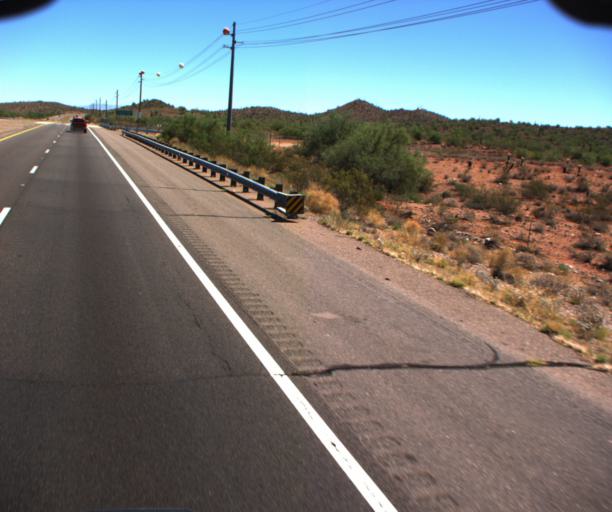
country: US
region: Arizona
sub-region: Maricopa County
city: Fountain Hills
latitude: 33.5497
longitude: -111.7220
